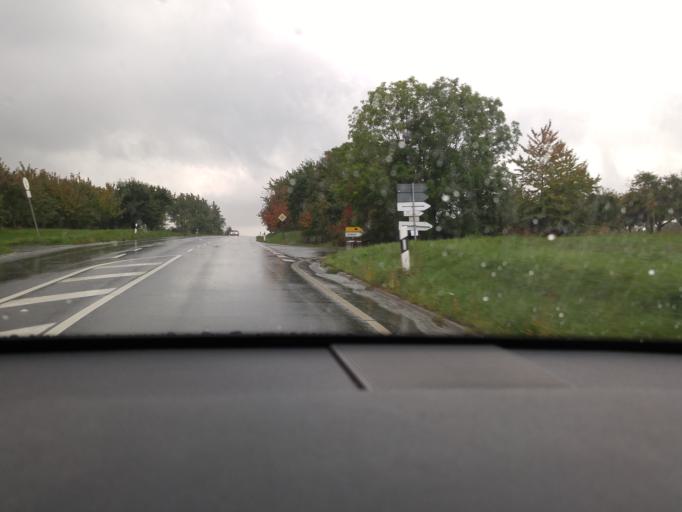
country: DE
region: Hesse
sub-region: Regierungsbezirk Darmstadt
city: Rosbach vor der Hohe
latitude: 50.3268
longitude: 8.7183
